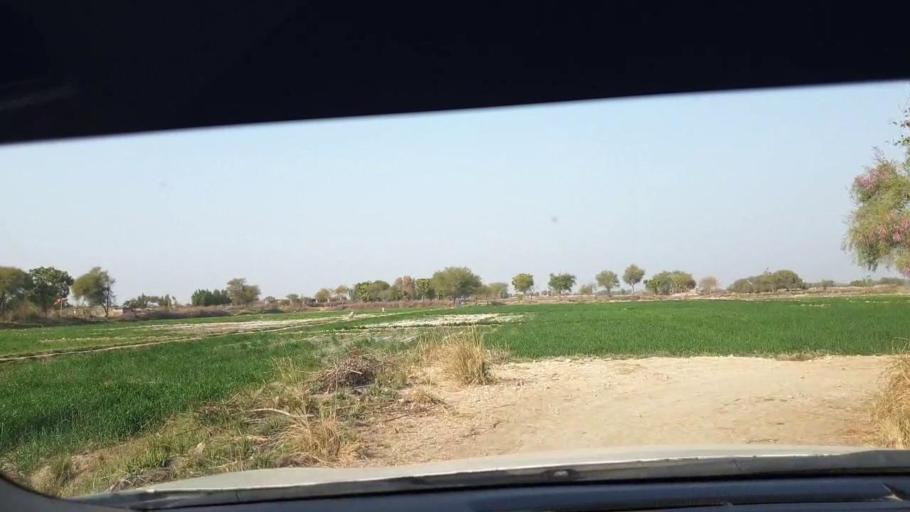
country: PK
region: Sindh
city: Berani
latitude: 25.8237
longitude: 68.7795
